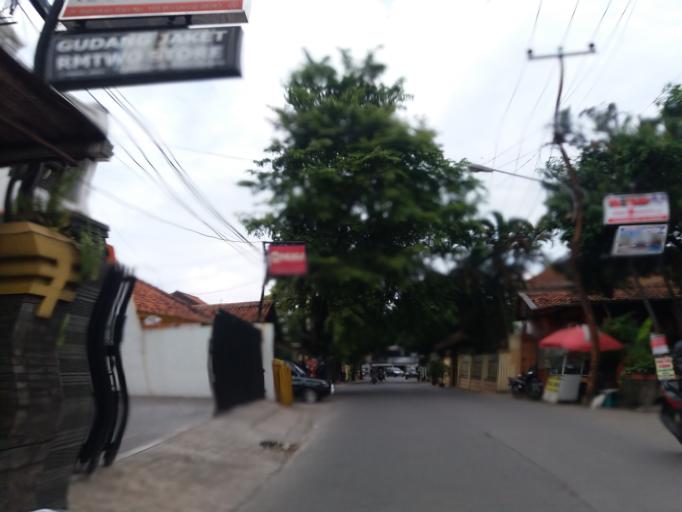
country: ID
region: West Java
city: Bandung
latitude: -6.9235
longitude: 107.6533
